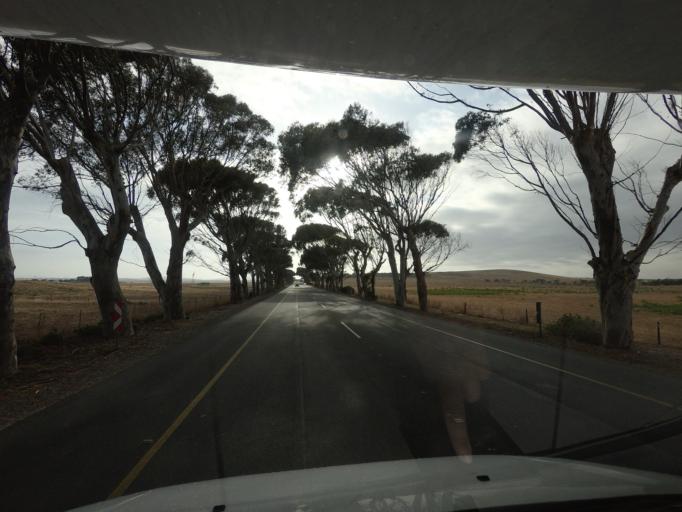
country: ZA
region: Western Cape
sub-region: City of Cape Town
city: Sunset Beach
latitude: -33.7253
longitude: 18.4683
